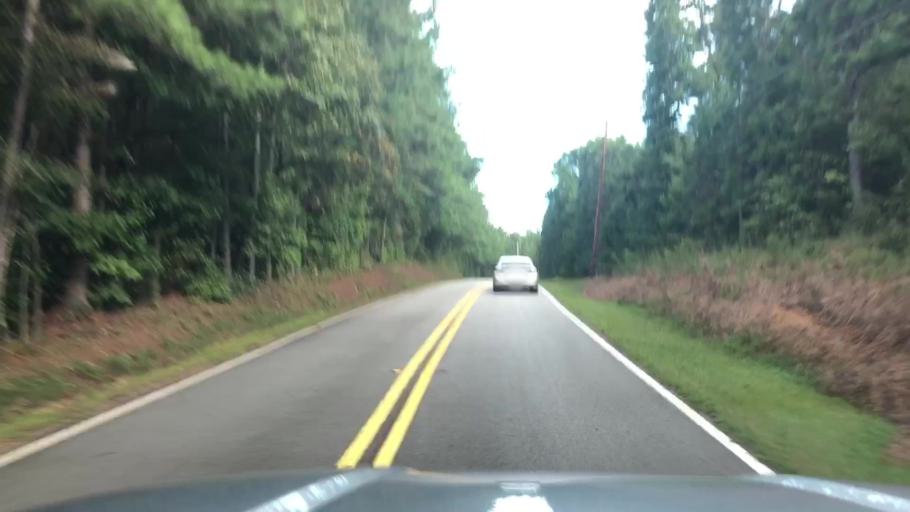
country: US
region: Georgia
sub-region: Paulding County
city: Dallas
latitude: 34.0418
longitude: -84.8653
